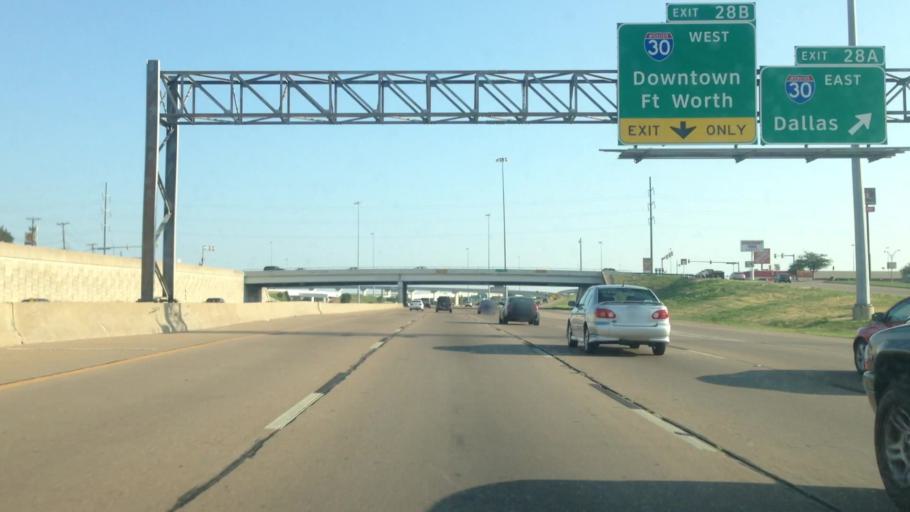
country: US
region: Texas
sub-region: Tarrant County
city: Richland Hills
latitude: 32.7684
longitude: -97.2129
